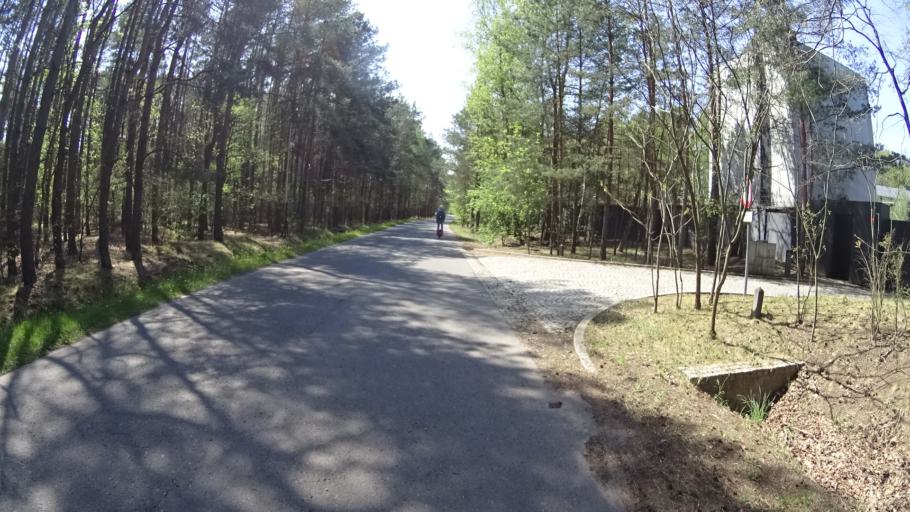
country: PL
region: Masovian Voivodeship
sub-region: Powiat warszawski zachodni
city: Truskaw
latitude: 52.2797
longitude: 20.7243
